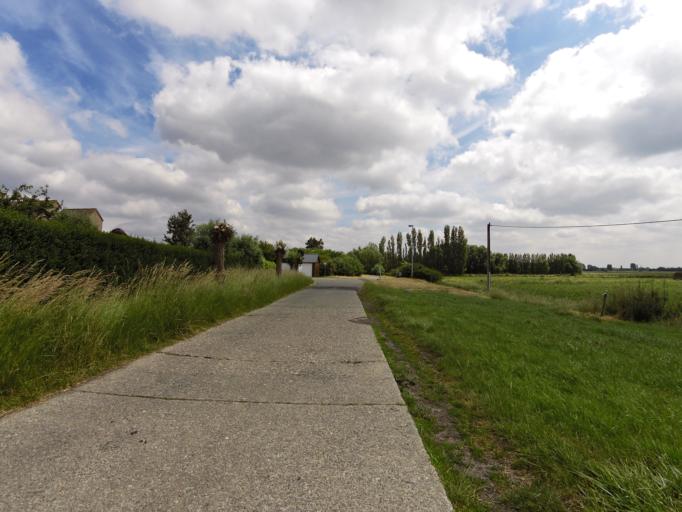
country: BE
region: Flanders
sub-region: Provincie West-Vlaanderen
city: Oudenburg
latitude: 51.1942
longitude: 2.9807
